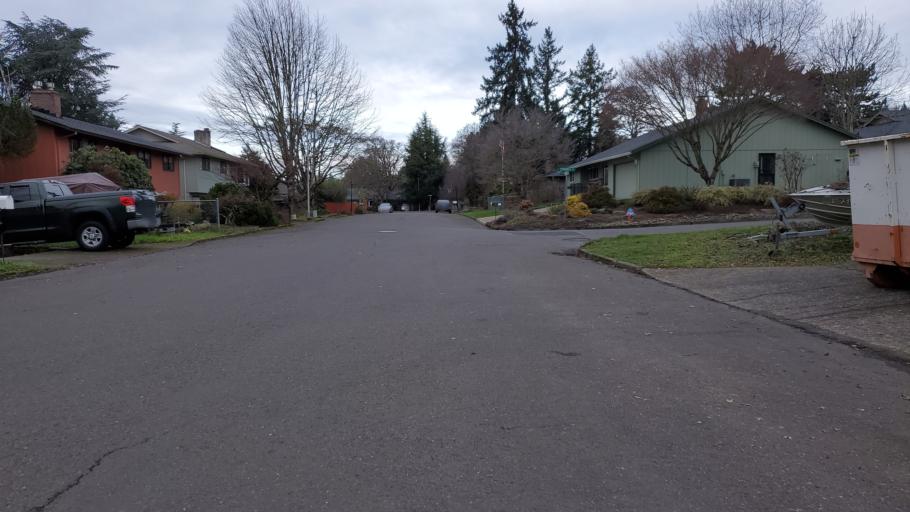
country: US
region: Oregon
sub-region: Clackamas County
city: Gladstone
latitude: 45.3894
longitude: -122.5934
